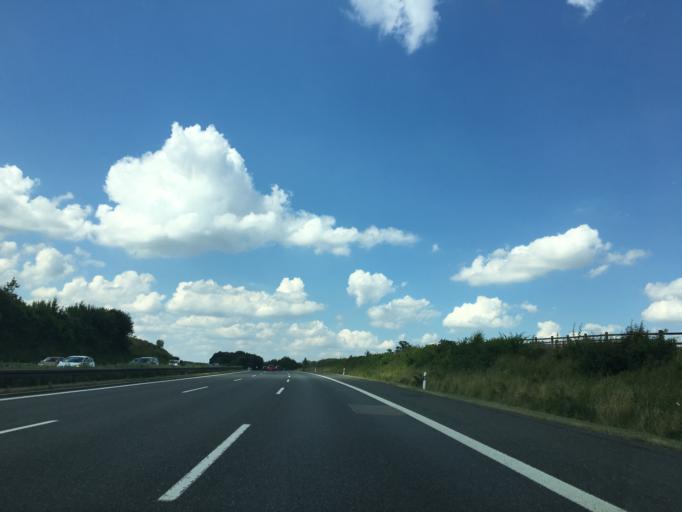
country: DE
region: Bavaria
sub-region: Upper Bavaria
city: Stammham
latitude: 48.8736
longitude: 11.4682
